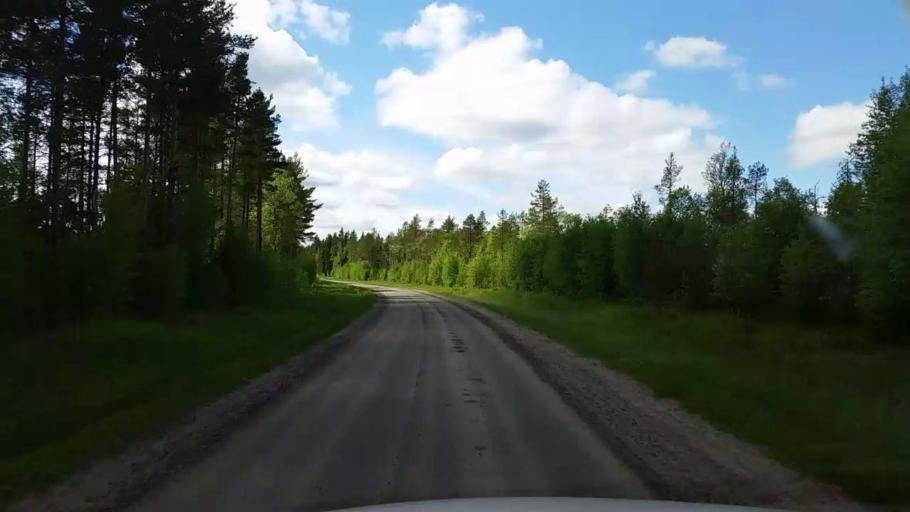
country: SE
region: Gaevleborg
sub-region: Ovanakers Kommun
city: Edsbyn
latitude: 61.5709
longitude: 15.9479
